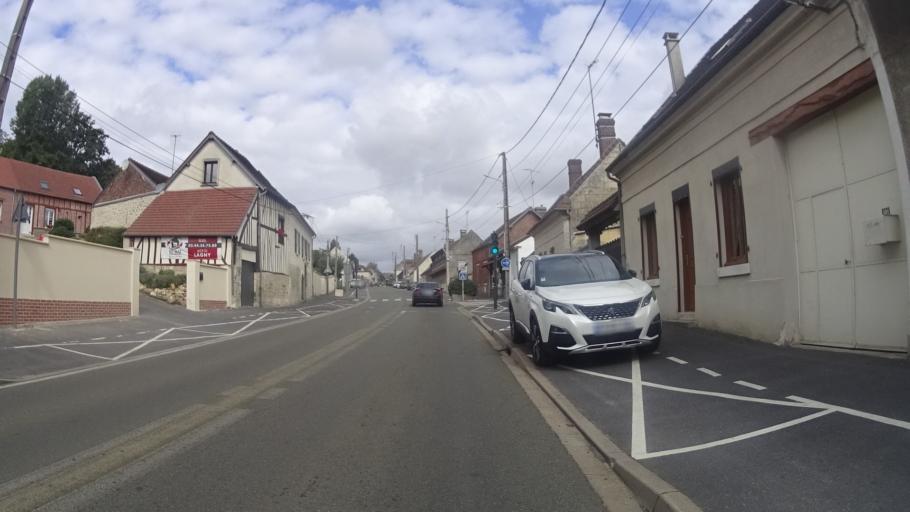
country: FR
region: Picardie
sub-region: Departement de l'Oise
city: Longueil-Annel
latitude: 49.4516
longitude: 2.8644
